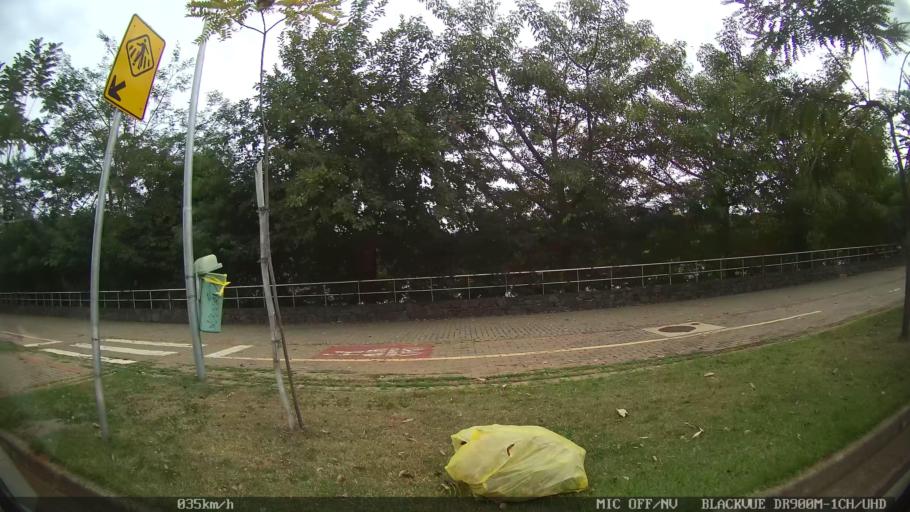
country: BR
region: Sao Paulo
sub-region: Piracicaba
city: Piracicaba
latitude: -22.7127
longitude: -47.6502
